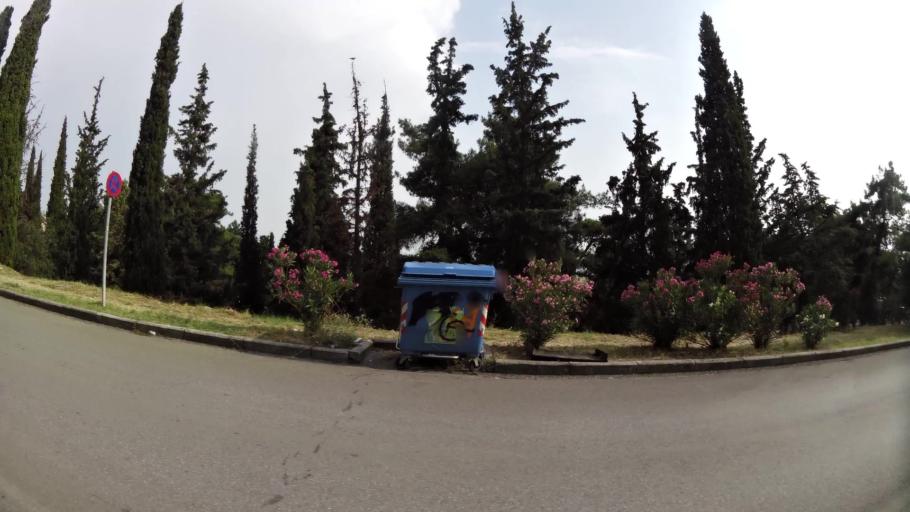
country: GR
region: Central Macedonia
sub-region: Nomos Thessalonikis
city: Oraiokastro
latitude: 40.7242
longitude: 22.9119
